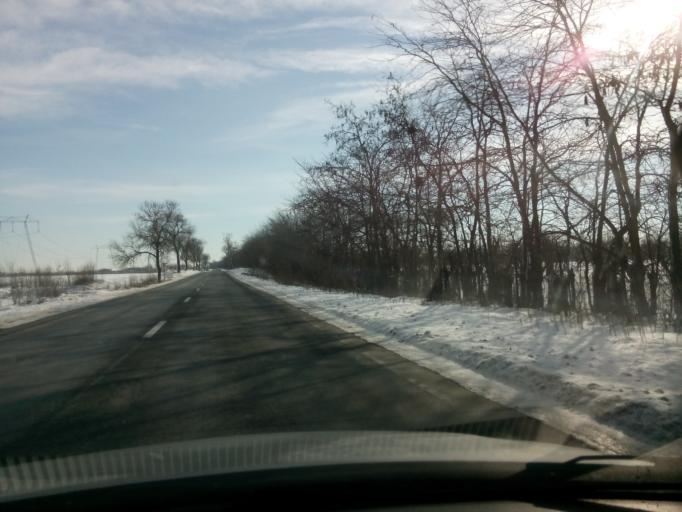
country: RO
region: Ilfov
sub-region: Comuna Glina
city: Glina
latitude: 44.3228
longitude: 26.2653
